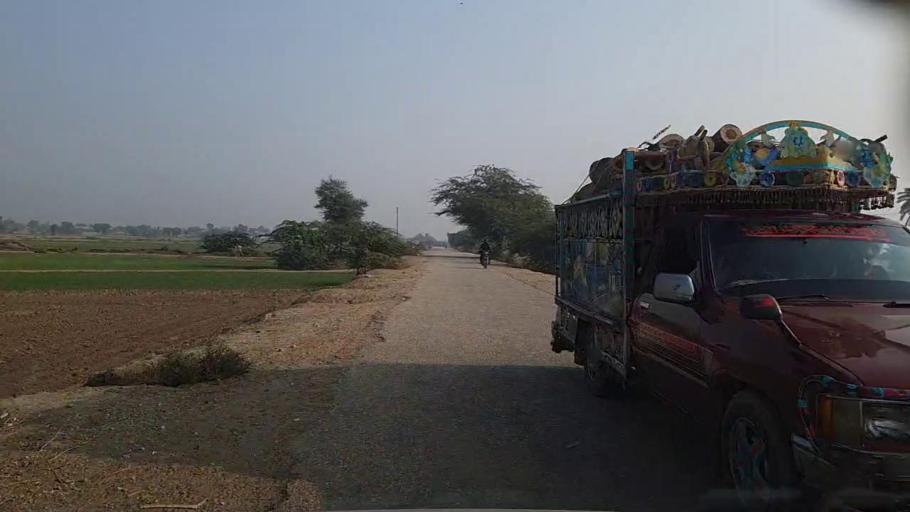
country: PK
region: Sindh
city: Kandiari
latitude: 27.0460
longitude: 68.4720
